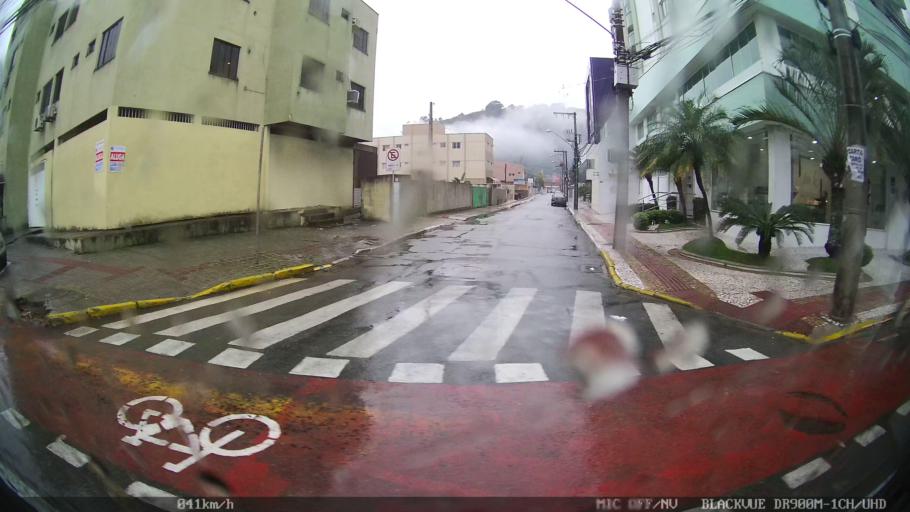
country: BR
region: Santa Catarina
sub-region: Itajai
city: Itajai
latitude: -26.9145
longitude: -48.6683
